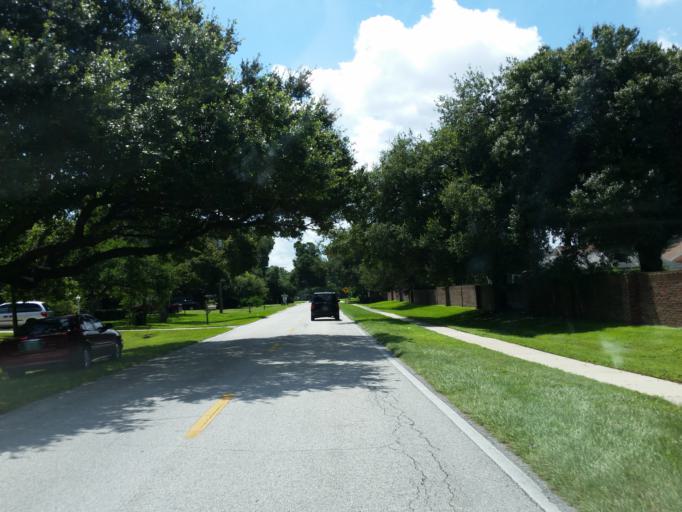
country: US
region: Florida
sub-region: Hillsborough County
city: Riverview
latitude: 27.8750
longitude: -82.3308
